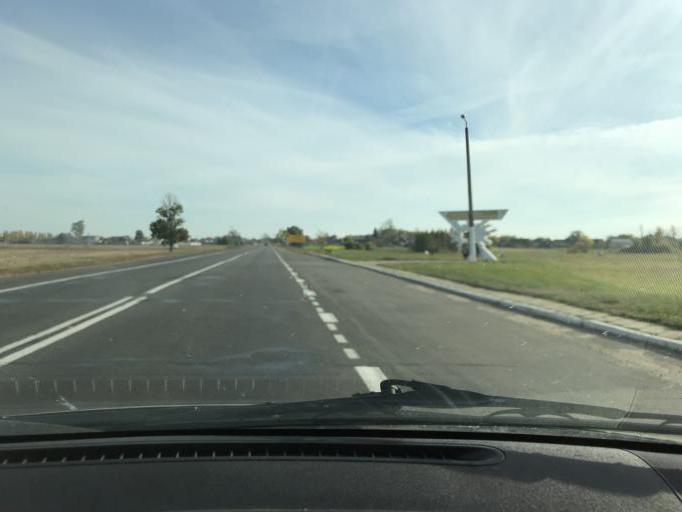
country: BY
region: Brest
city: Asnyezhytsy
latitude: 52.1811
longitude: 26.0835
